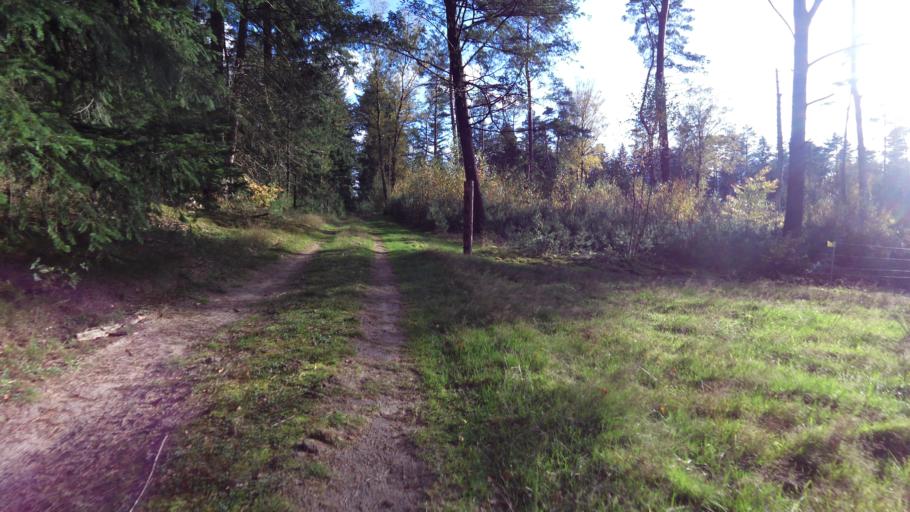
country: NL
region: Gelderland
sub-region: Gemeente Nunspeet
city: Nunspeet
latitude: 52.3476
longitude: 5.8498
